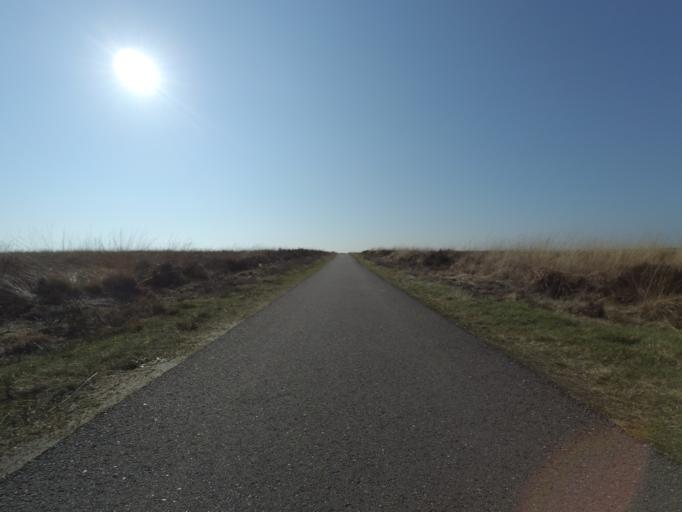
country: NL
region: Gelderland
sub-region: Gemeente Renkum
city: Wolfheze
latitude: 52.0528
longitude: 5.8244
